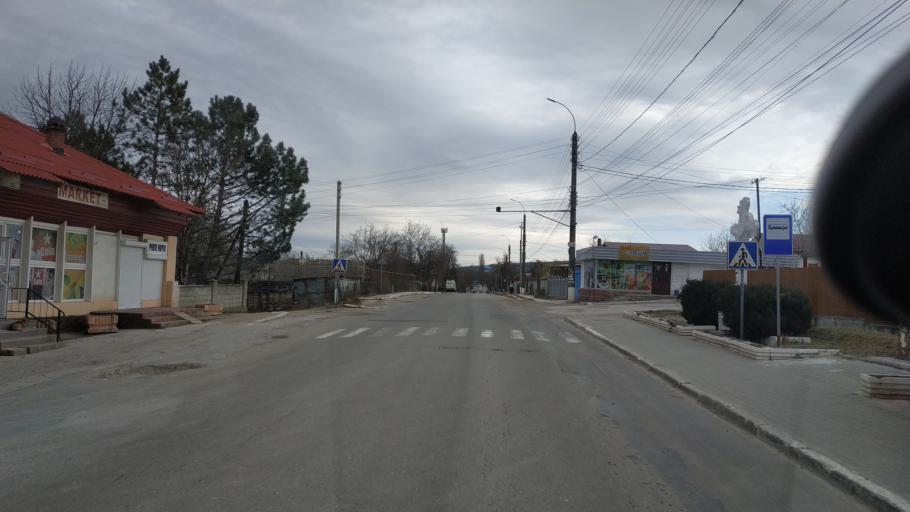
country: MD
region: Chisinau
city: Vadul lui Voda
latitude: 47.0935
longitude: 29.0738
